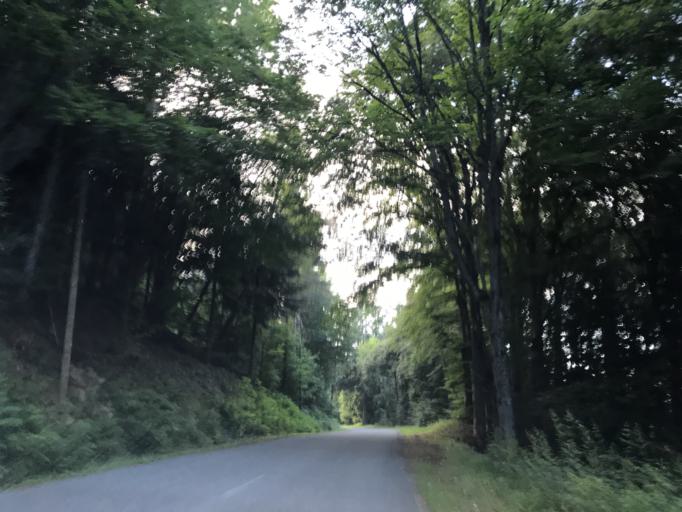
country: FR
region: Rhone-Alpes
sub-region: Departement de la Loire
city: Noiretable
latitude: 45.7463
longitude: 3.8437
